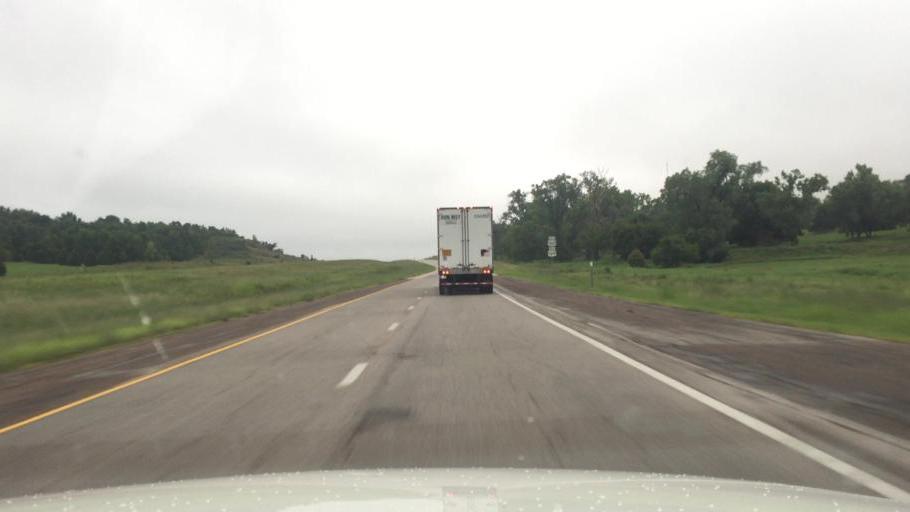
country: US
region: Kansas
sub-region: Montgomery County
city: Cherryvale
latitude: 37.2202
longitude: -95.5857
